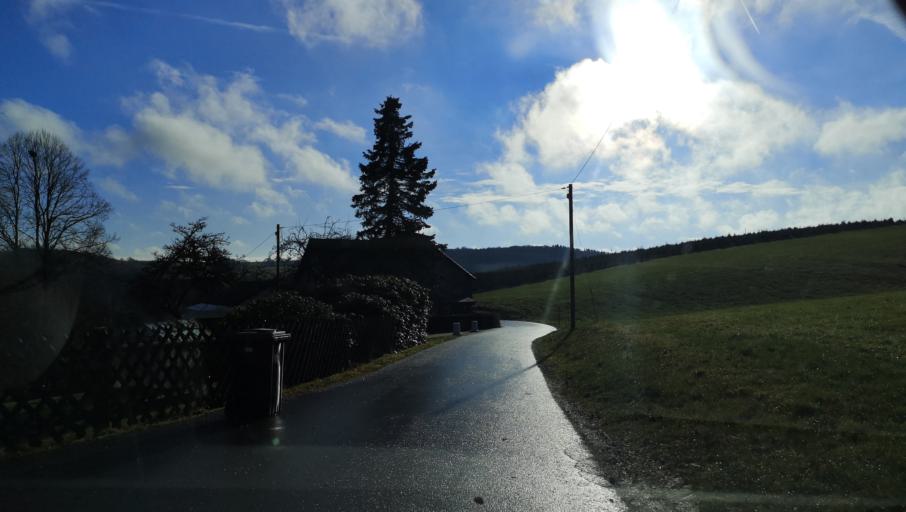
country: DE
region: North Rhine-Westphalia
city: Radevormwald
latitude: 51.1877
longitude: 7.4134
